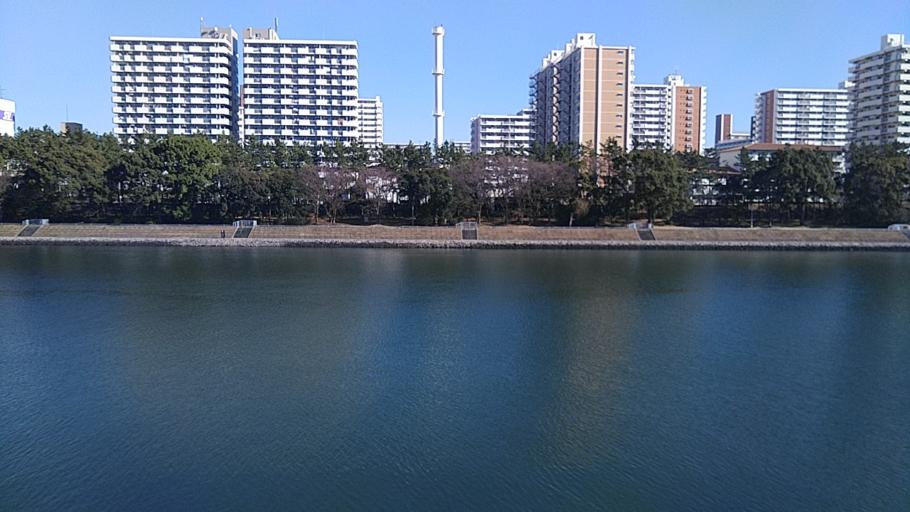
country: JP
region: Kanagawa
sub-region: Kawasaki-shi
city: Kawasaki
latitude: 35.5987
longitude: 139.7473
